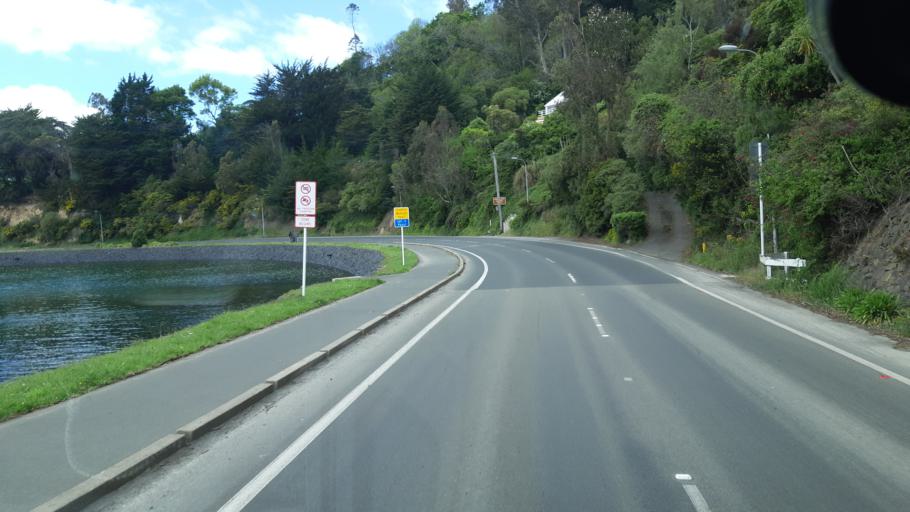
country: NZ
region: Otago
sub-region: Dunedin City
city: Portobello
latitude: -45.8749
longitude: 170.5828
